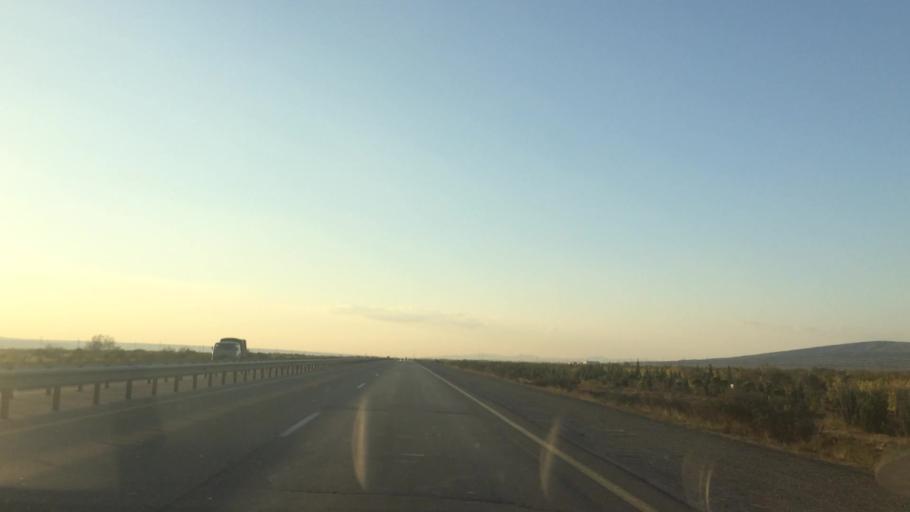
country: AZ
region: Baki
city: Qobustan
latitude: 39.9528
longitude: 49.3167
